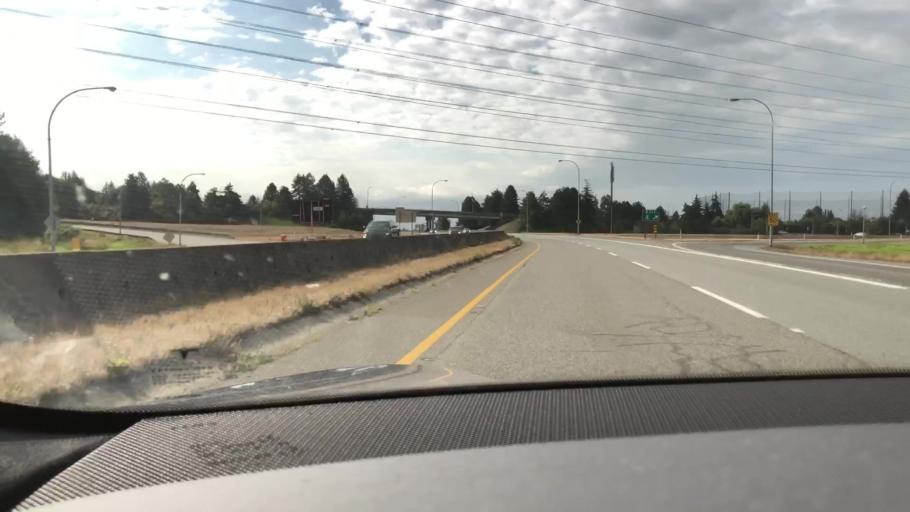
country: CA
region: British Columbia
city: Delta
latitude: 49.1224
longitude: -122.9278
